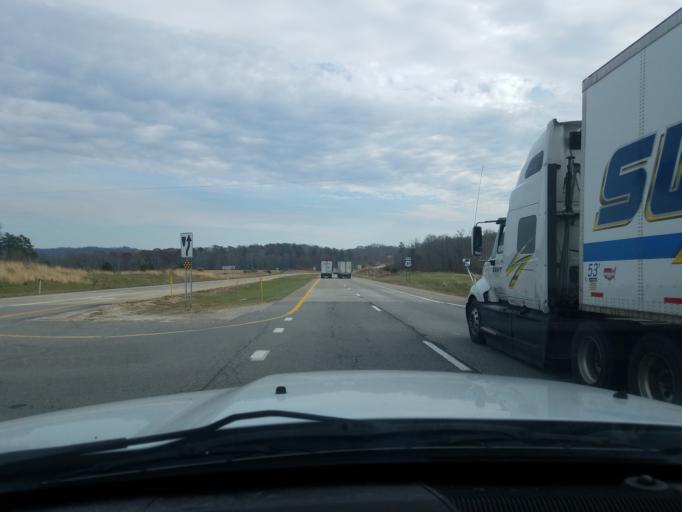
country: US
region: West Virginia
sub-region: Putnam County
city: Eleanor
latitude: 38.5487
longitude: -81.9802
